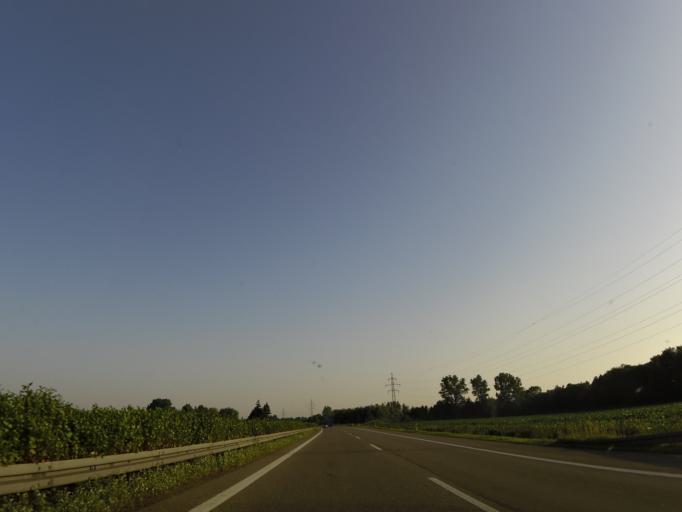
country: DE
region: Baden-Wuerttemberg
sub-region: Tuebingen Region
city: Dettingen an der Iller
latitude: 48.0969
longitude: 10.1335
